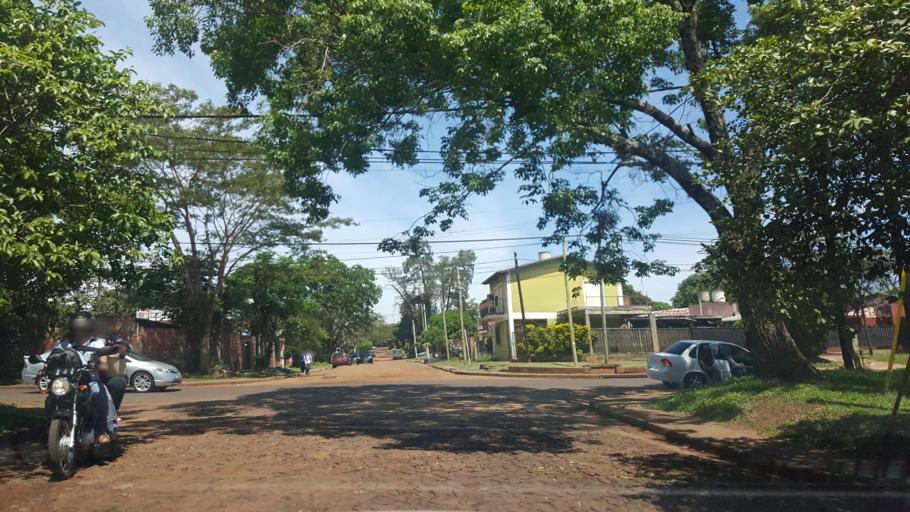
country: AR
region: Misiones
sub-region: Departamento de Capital
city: Posadas
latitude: -27.3862
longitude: -55.9105
